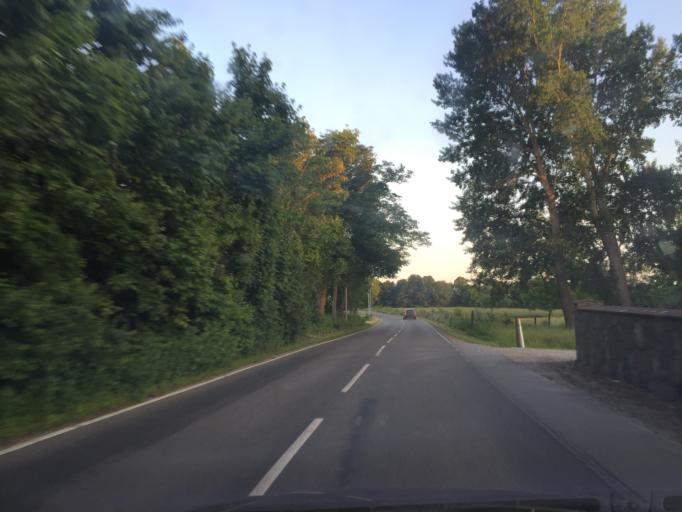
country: DK
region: Capital Region
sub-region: Hoje-Taastrup Kommune
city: Taastrup
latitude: 55.6909
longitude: 12.2457
